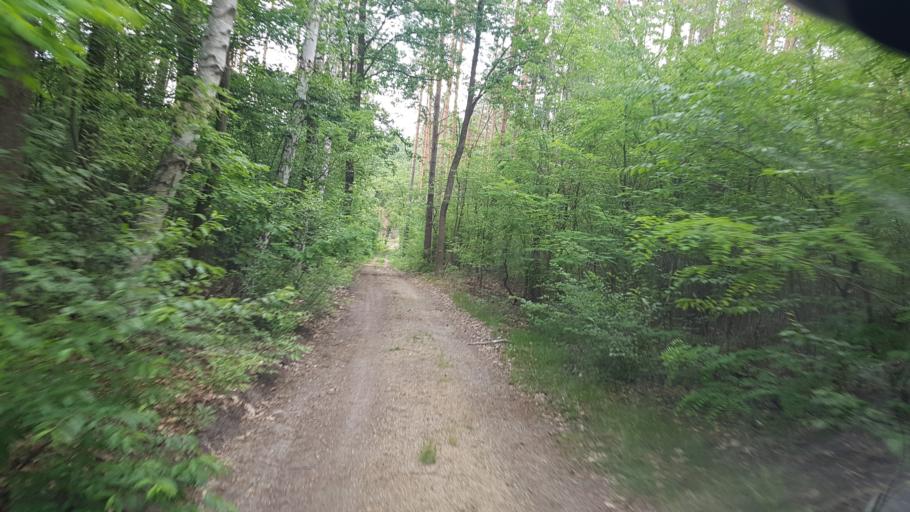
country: DE
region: Brandenburg
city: Hohenleipisch
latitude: 51.5100
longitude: 13.5686
